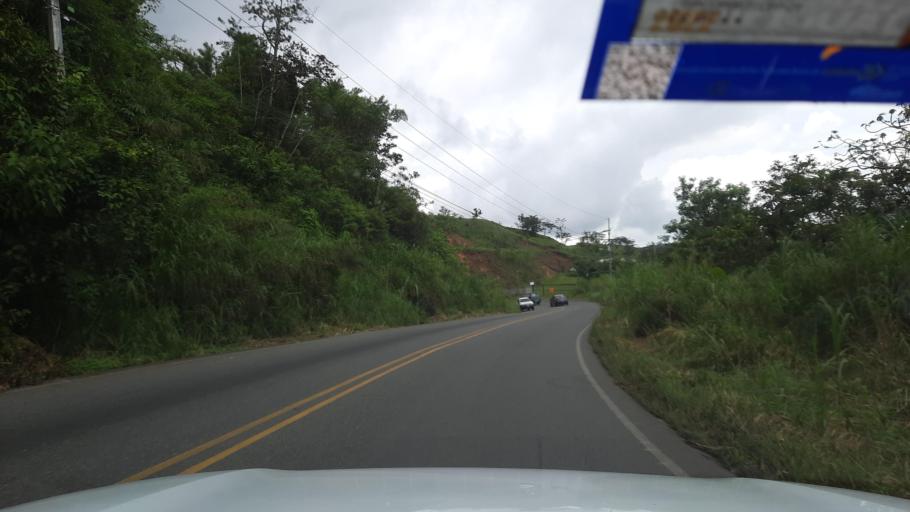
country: CR
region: Alajuela
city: San Rafael
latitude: 10.0406
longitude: -84.5056
